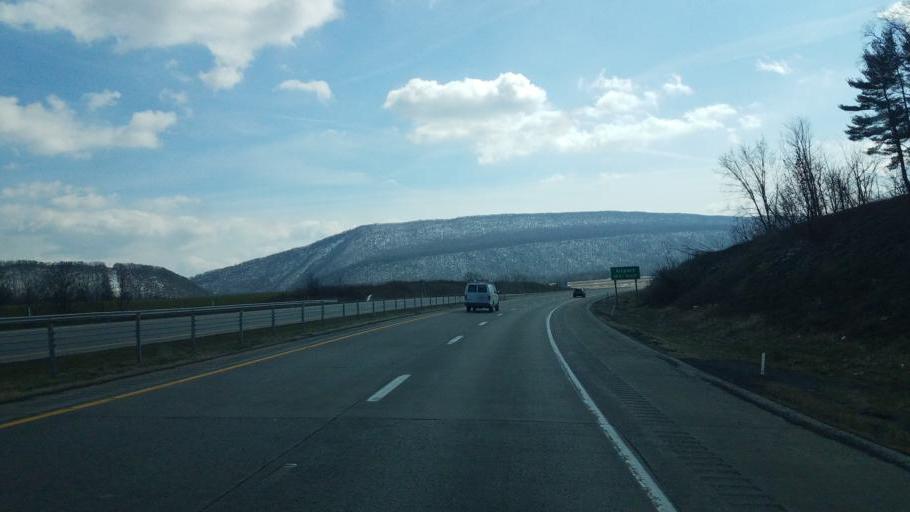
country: US
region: Pennsylvania
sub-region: Mifflin County
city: Church Hill
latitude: 40.6751
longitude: -77.6037
